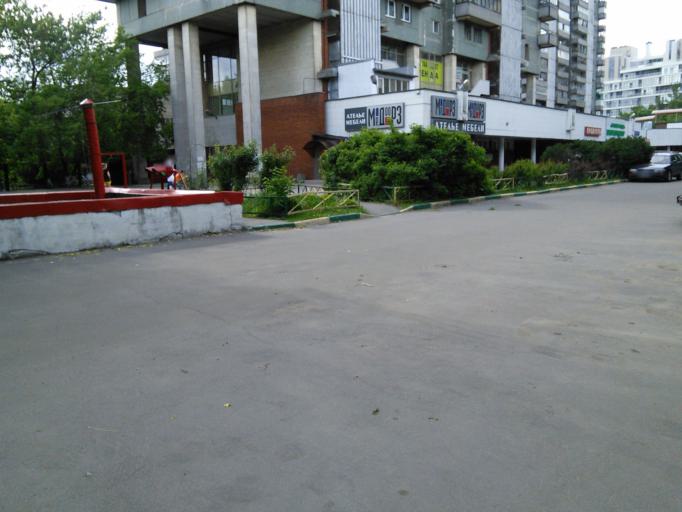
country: RU
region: Moskovskaya
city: Levoberezhnyy
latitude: 55.8302
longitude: 37.4877
